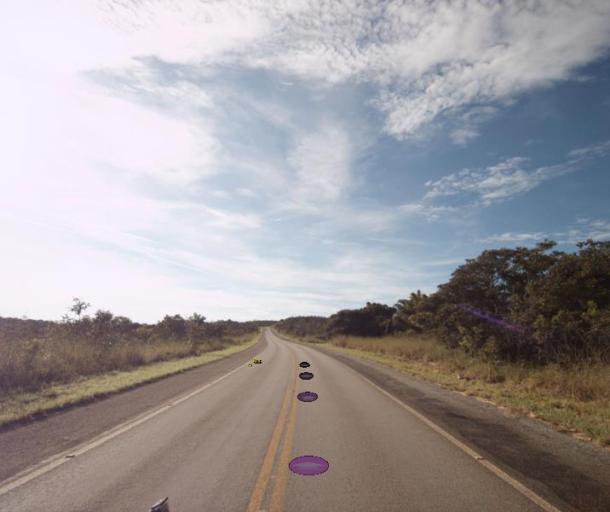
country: BR
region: Goias
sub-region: Pirenopolis
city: Pirenopolis
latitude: -15.7702
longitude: -48.5633
